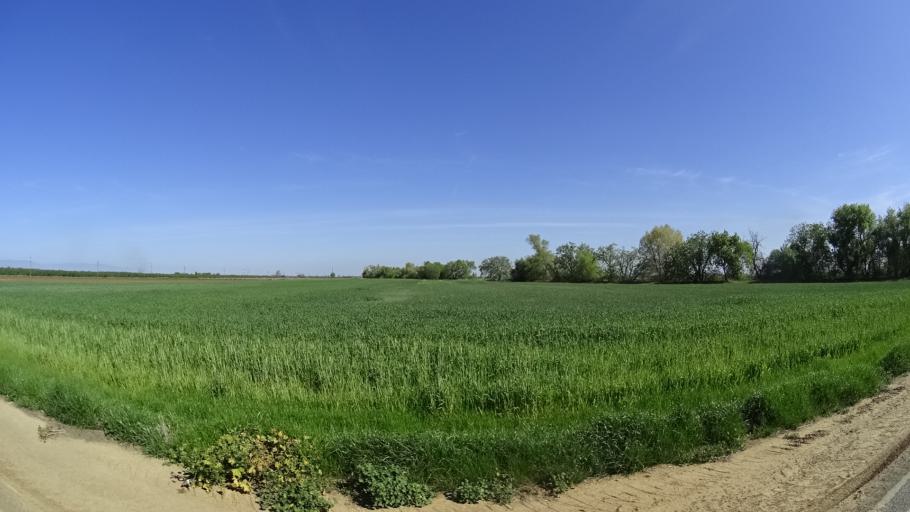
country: US
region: California
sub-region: Glenn County
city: Willows
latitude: 39.5387
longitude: -122.1830
